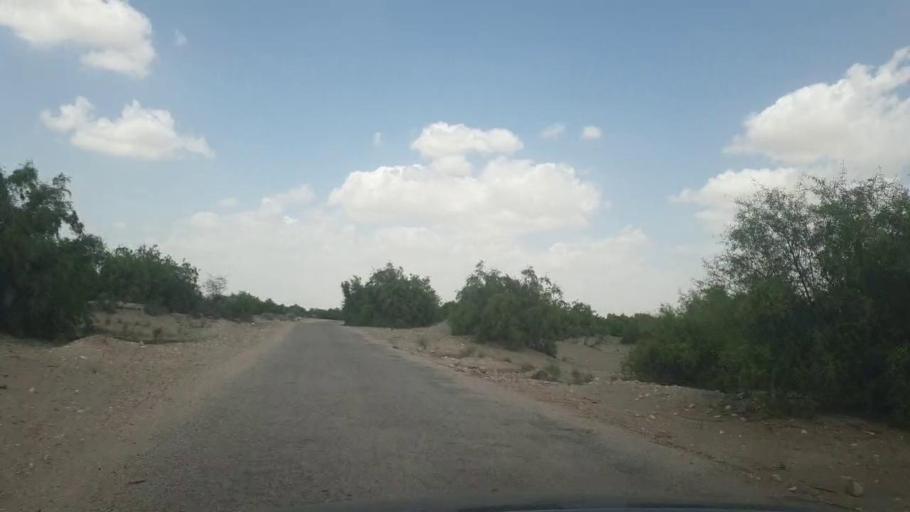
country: PK
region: Sindh
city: Kot Diji
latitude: 27.2203
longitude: 69.1031
